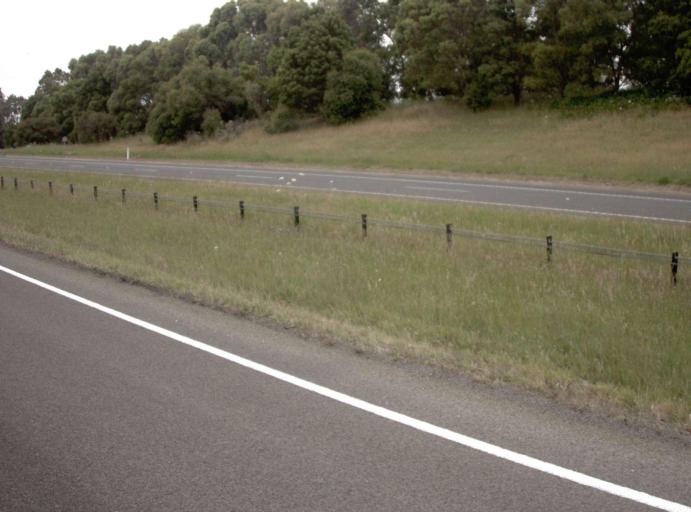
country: AU
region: Victoria
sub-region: Baw Baw
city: Warragul
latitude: -38.1474
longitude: 145.8858
